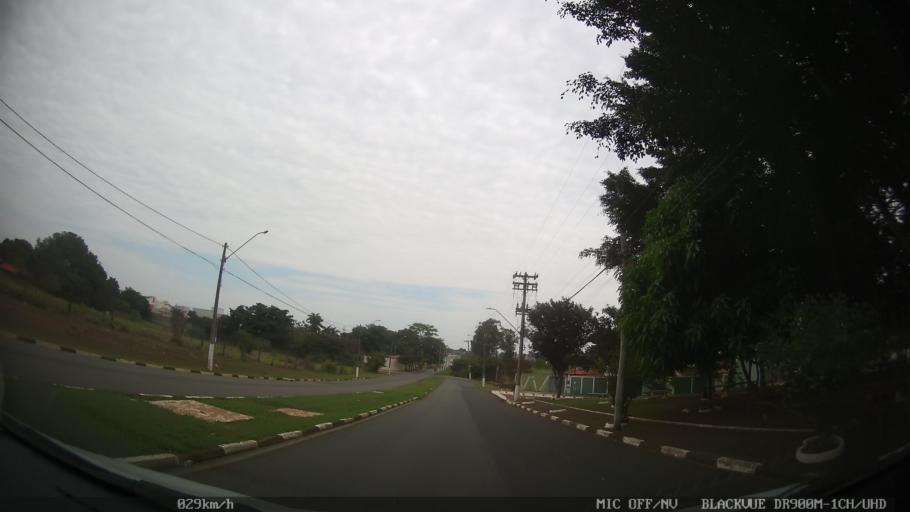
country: BR
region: Sao Paulo
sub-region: Paulinia
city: Paulinia
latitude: -22.7340
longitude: -47.1823
